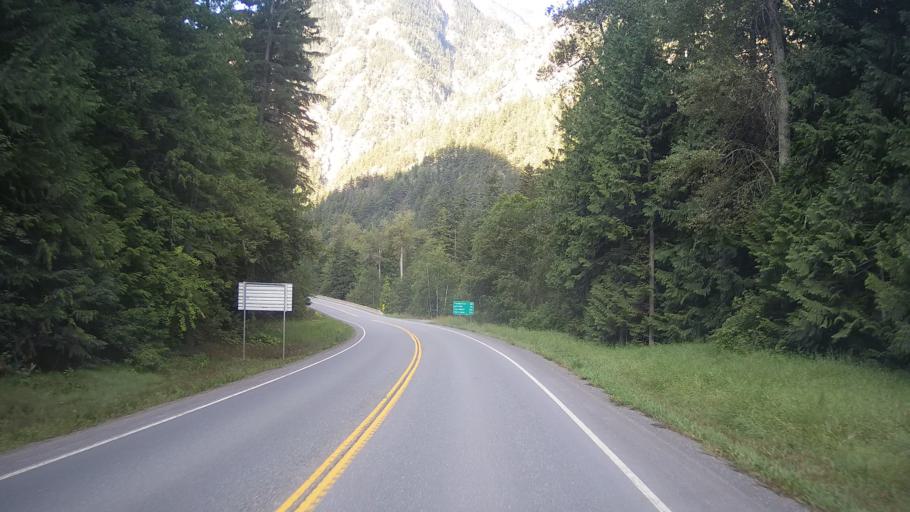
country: CA
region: British Columbia
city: Lillooet
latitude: 50.6243
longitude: -122.1009
